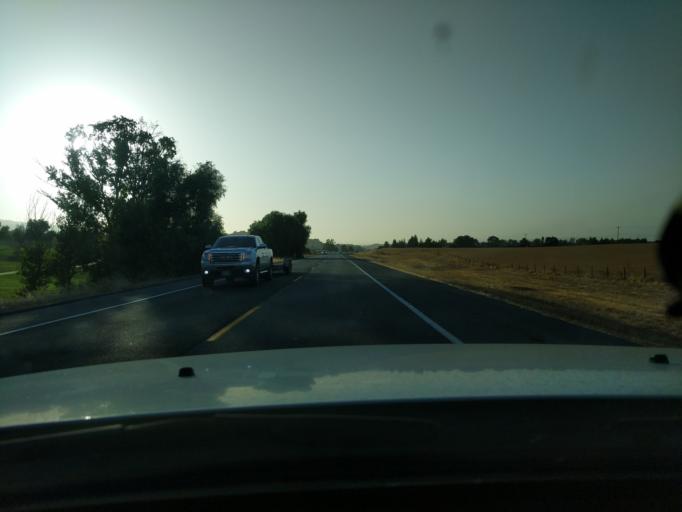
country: US
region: California
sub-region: San Benito County
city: Ridgemark
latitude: 36.8153
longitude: -121.3577
